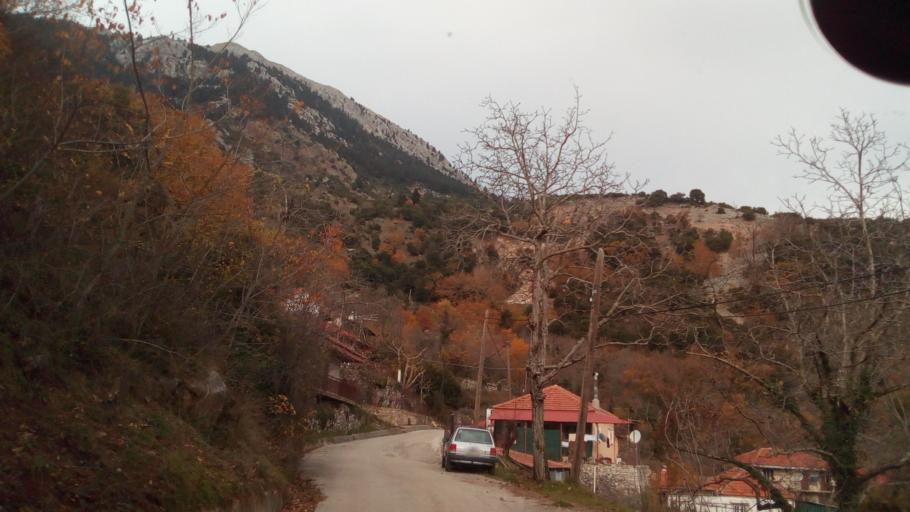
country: GR
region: West Greece
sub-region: Nomos Aitolias kai Akarnanias
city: Thermo
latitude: 38.6796
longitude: 21.8961
